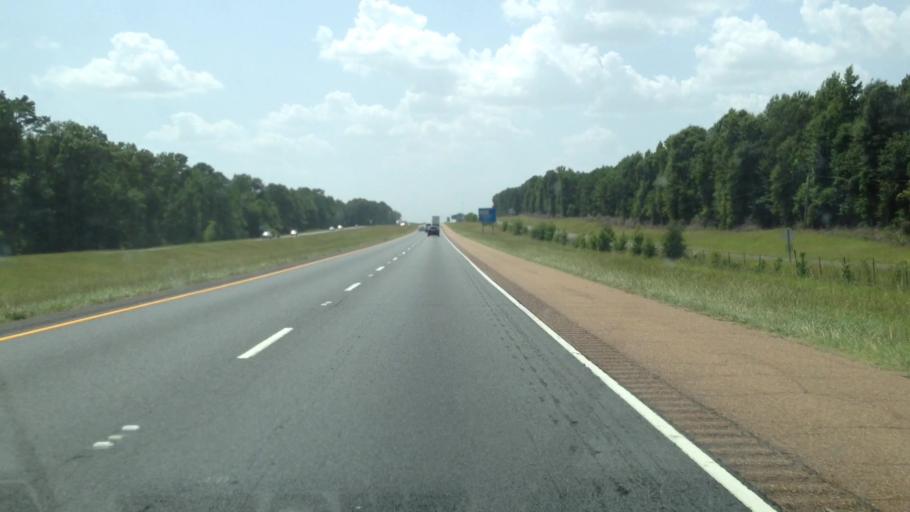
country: US
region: Louisiana
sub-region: Bienville Parish
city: Arcadia
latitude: 32.5605
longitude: -92.8951
